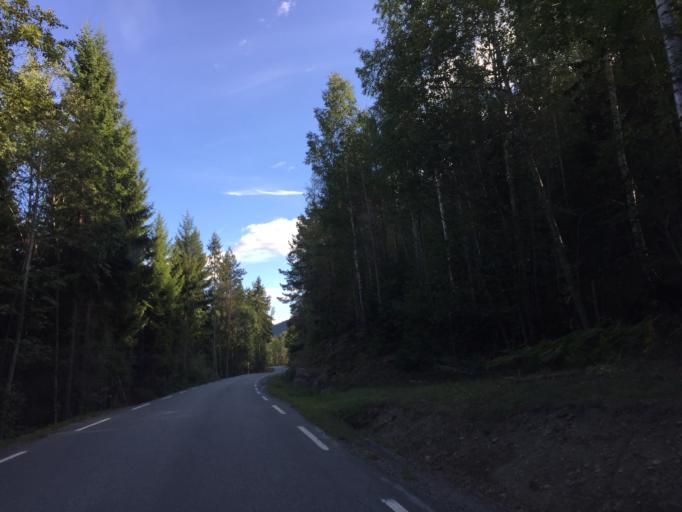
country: NO
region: Buskerud
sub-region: Ovre Eiker
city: Hokksund
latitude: 59.6499
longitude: 9.9181
